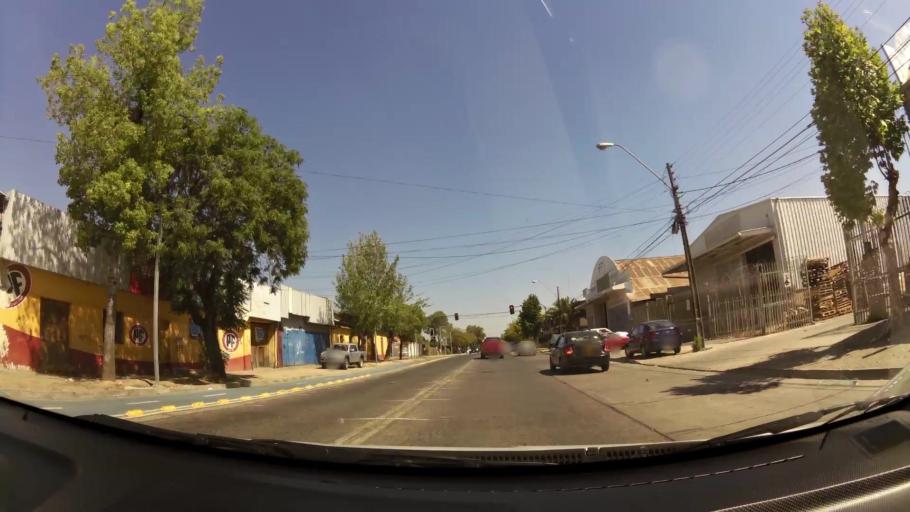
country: CL
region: Maule
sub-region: Provincia de Talca
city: Talca
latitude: -35.4185
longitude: -71.6492
